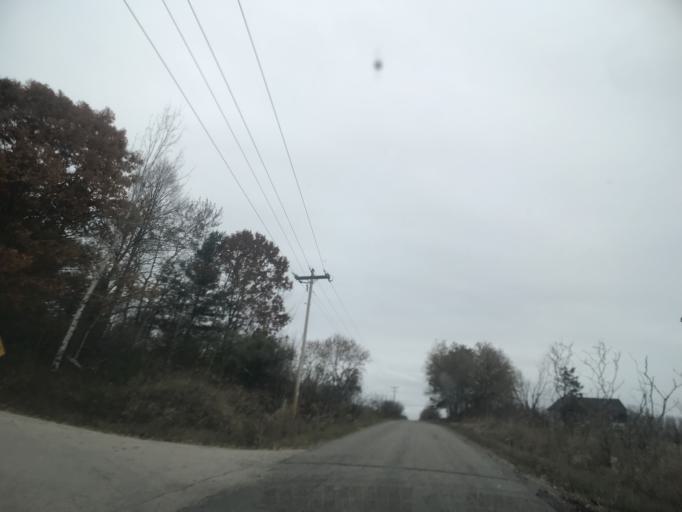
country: US
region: Wisconsin
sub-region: Menominee County
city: Legend Lake
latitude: 45.1711
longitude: -88.4558
